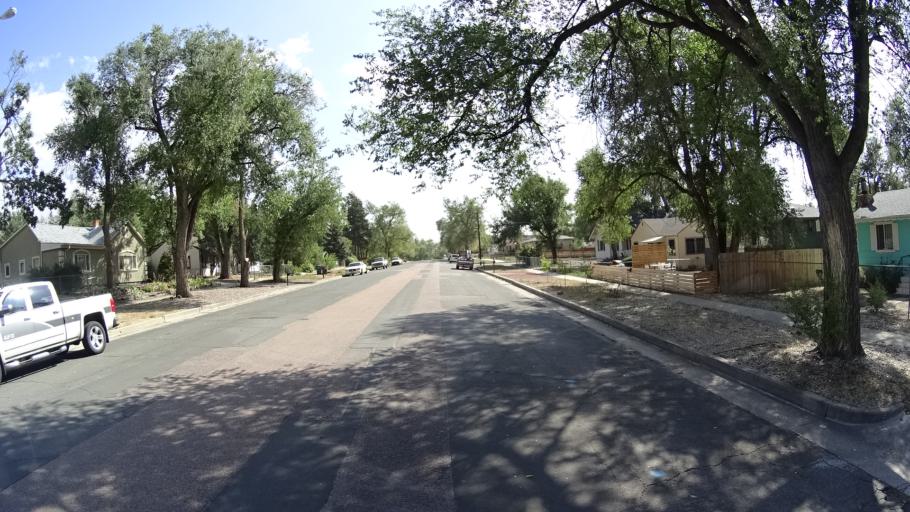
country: US
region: Colorado
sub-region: El Paso County
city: Colorado Springs
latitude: 38.8238
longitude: -104.8036
